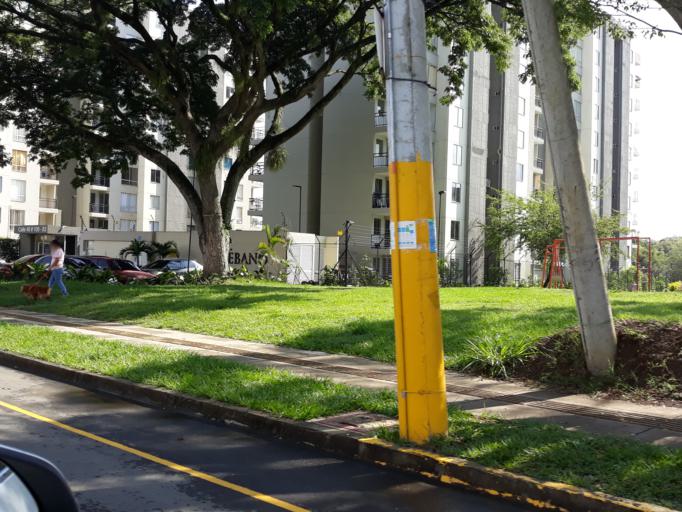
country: CO
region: Valle del Cauca
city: Cali
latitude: 3.3573
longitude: -76.5159
